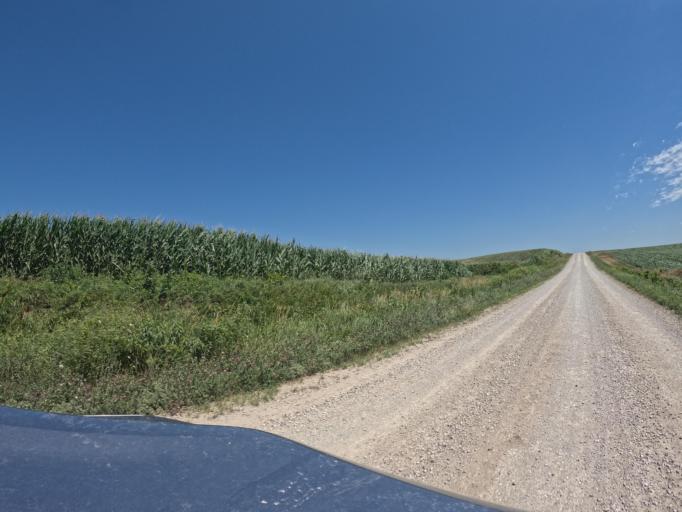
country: US
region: Iowa
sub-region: Keokuk County
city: Sigourney
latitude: 41.4523
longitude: -92.3647
